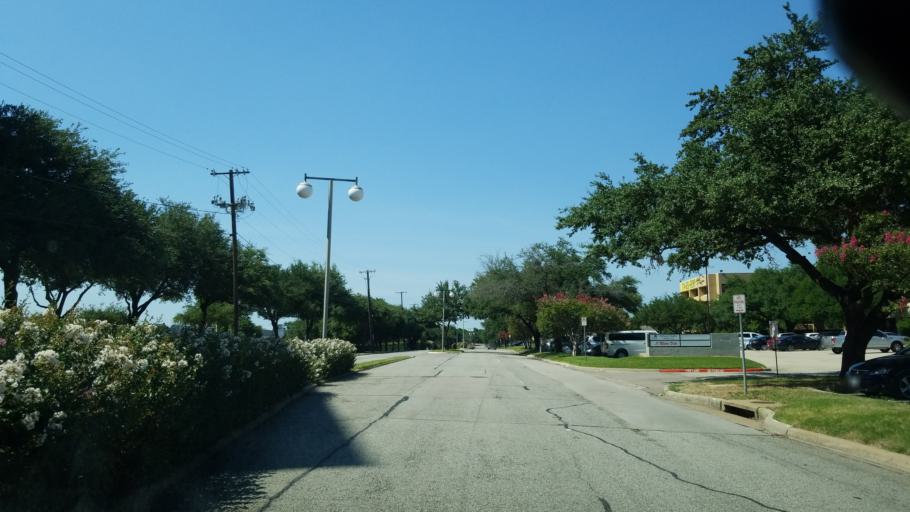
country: US
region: Texas
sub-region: Dallas County
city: Farmers Branch
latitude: 32.9118
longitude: -96.8915
